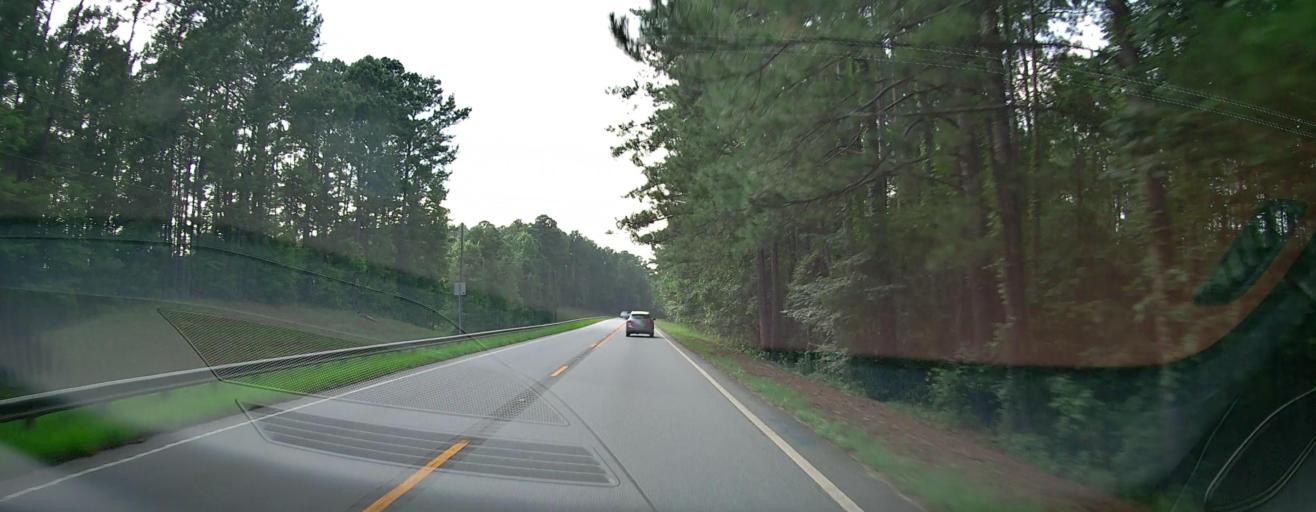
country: US
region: Georgia
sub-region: Monroe County
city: Forsyth
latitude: 33.0376
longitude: -83.7527
